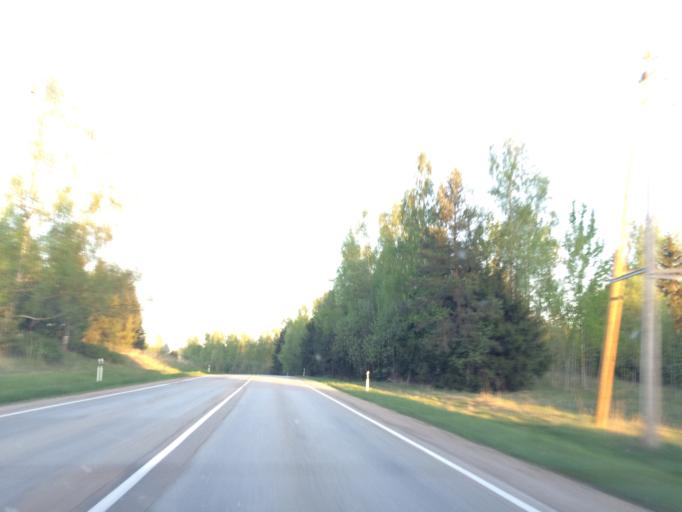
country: LV
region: Ludzas Rajons
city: Ludza
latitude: 56.5362
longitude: 27.5799
